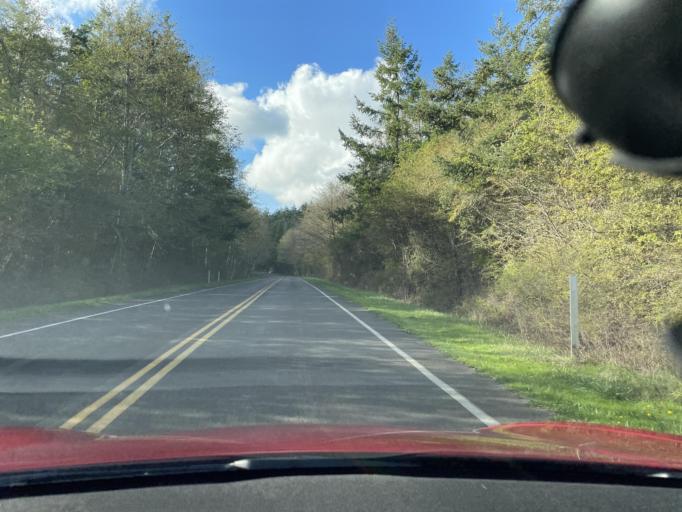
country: US
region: Washington
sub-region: San Juan County
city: Friday Harbor
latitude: 48.4686
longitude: -123.0131
